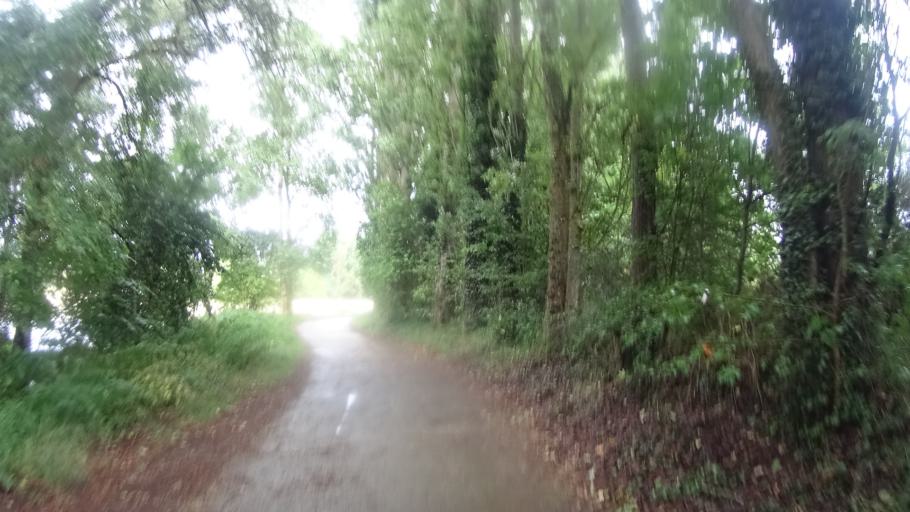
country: FR
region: Centre
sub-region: Departement du Loiret
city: Saint-Jean-de-Braye
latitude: 47.9005
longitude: 1.9552
